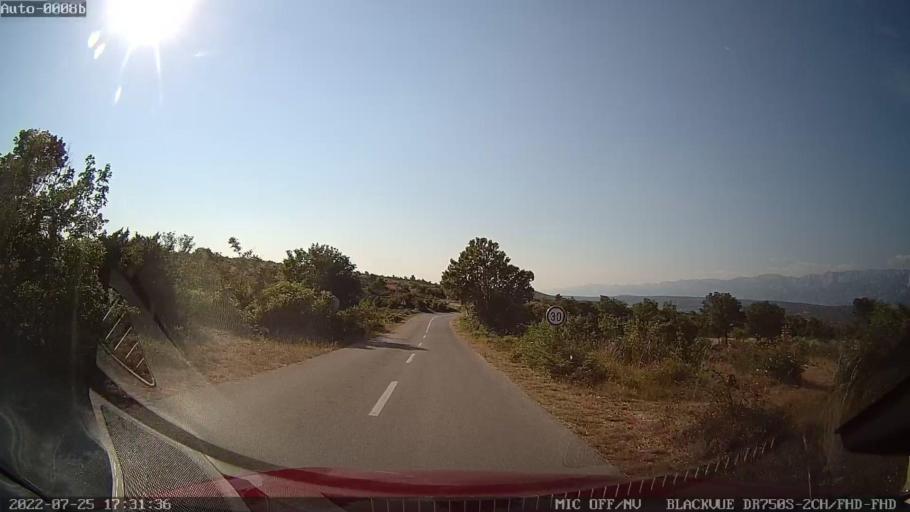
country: HR
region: Zadarska
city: Posedarje
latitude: 44.1713
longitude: 15.4982
